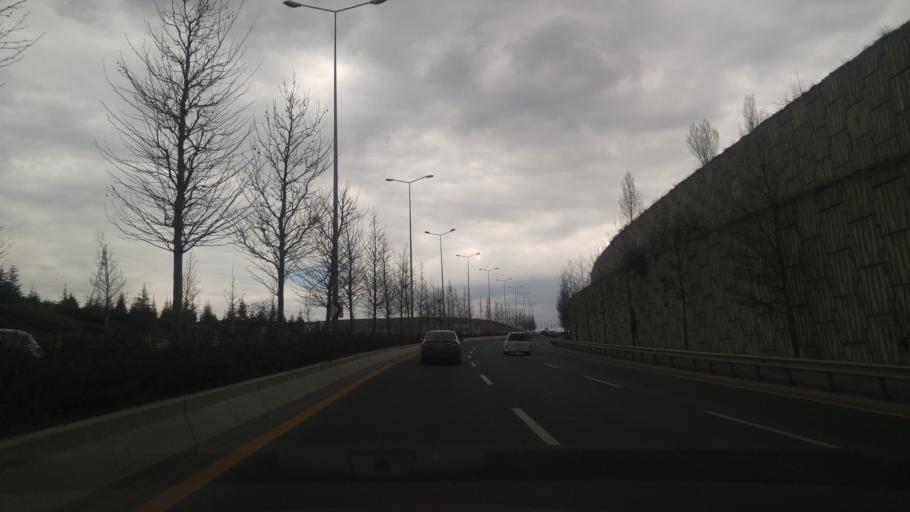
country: TR
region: Ankara
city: Mamak
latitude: 39.8878
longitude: 32.9126
